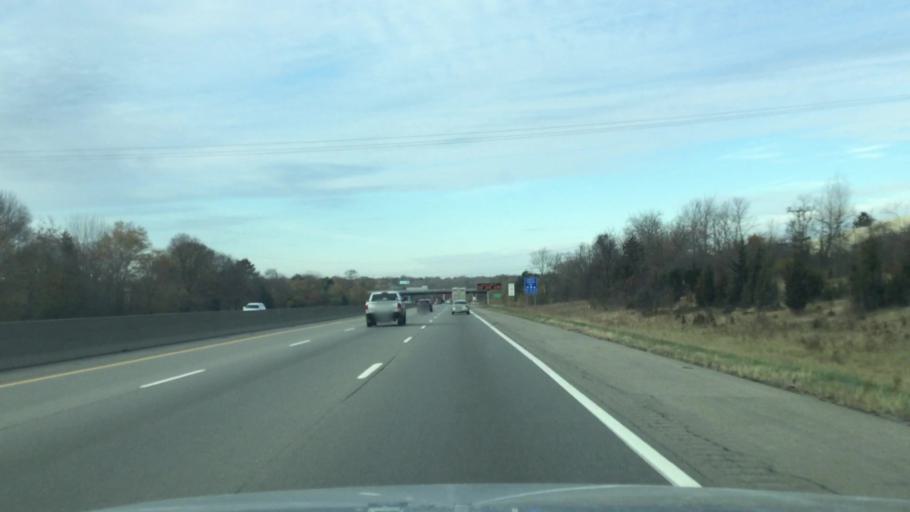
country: US
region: Michigan
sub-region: Washtenaw County
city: Ypsilanti
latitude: 42.2317
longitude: -83.5937
